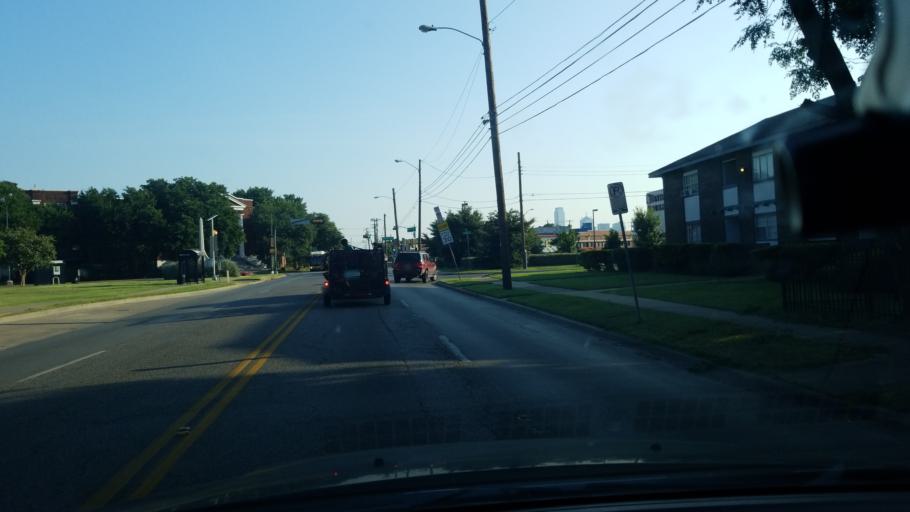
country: US
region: Texas
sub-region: Dallas County
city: Dallas
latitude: 32.7464
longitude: -96.8156
